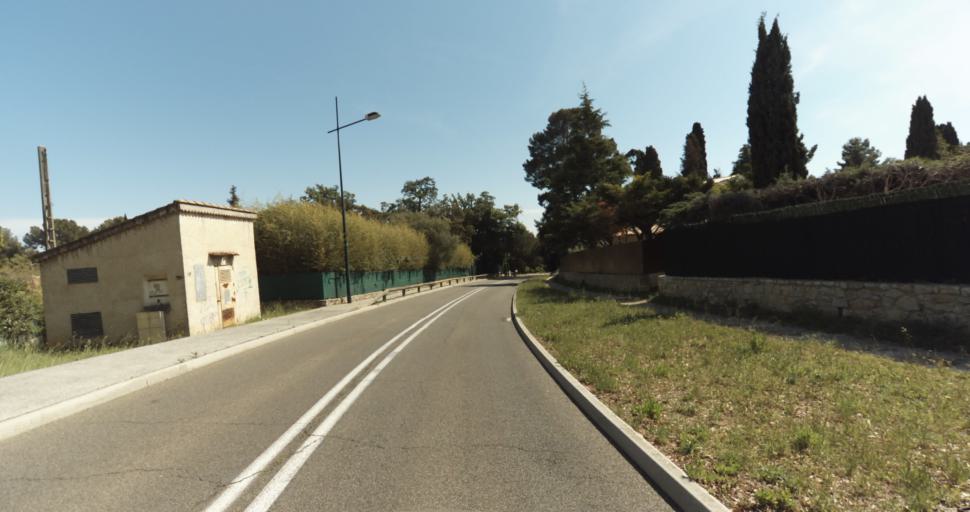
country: FR
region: Provence-Alpes-Cote d'Azur
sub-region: Departement du Var
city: Hyeres
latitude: 43.0947
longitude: 6.1247
